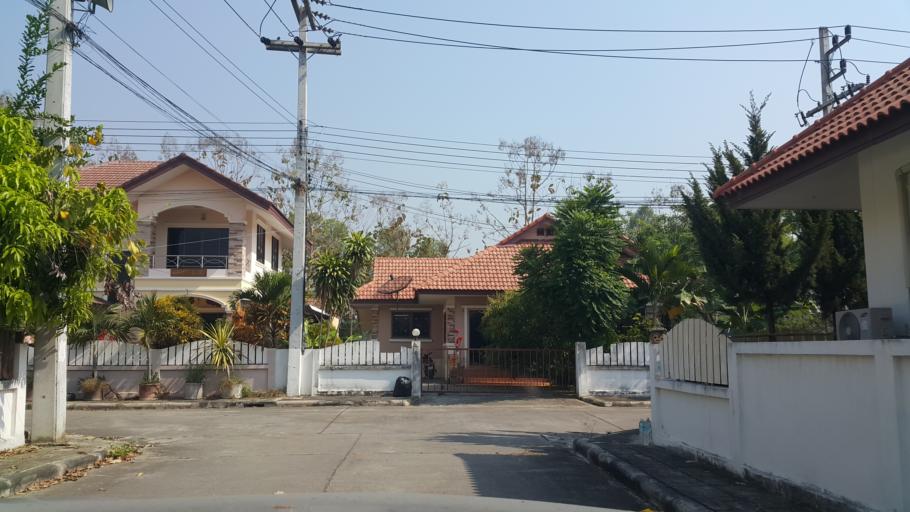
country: TH
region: Chiang Mai
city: San Kamphaeng
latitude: 18.7793
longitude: 99.0805
